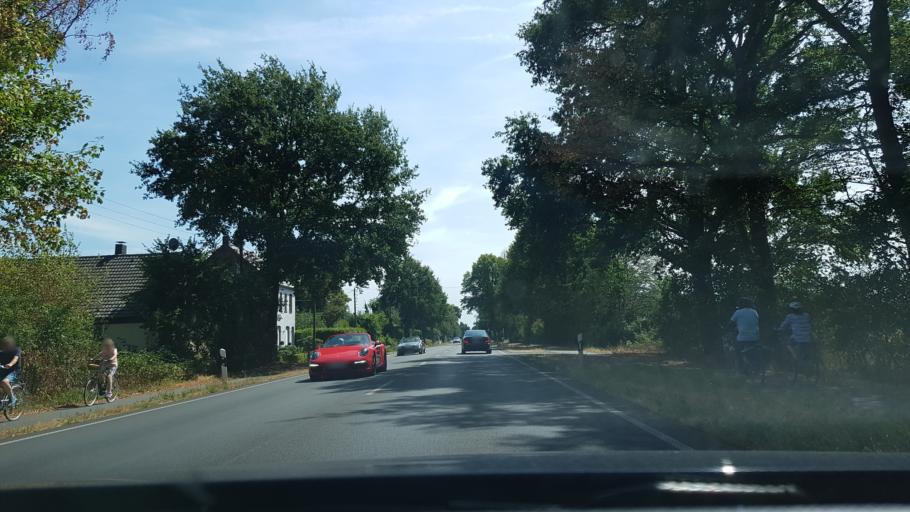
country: DE
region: North Rhine-Westphalia
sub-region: Regierungsbezirk Dusseldorf
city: Voerde
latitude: 51.5879
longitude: 6.7180
